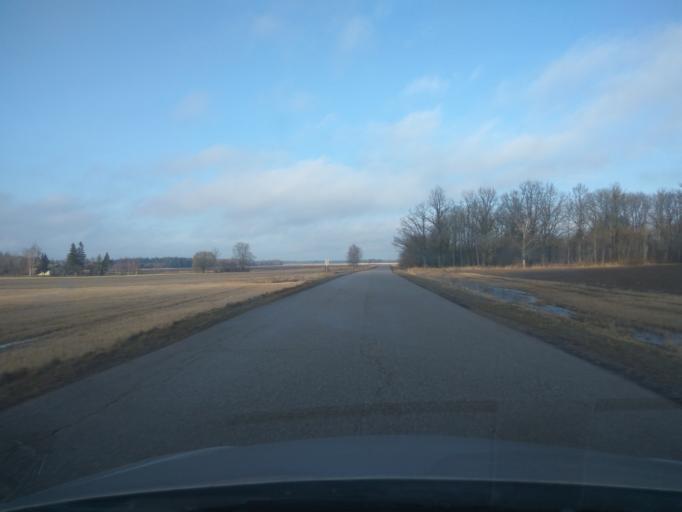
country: LV
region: Saldus Rajons
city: Saldus
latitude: 56.7985
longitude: 22.3818
